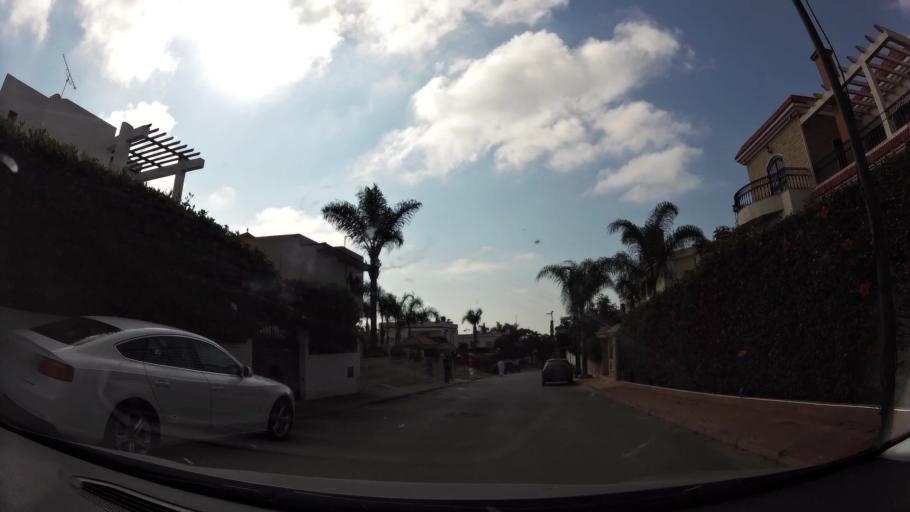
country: MA
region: Rabat-Sale-Zemmour-Zaer
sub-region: Skhirate-Temara
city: Temara
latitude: 33.9551
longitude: -6.8775
